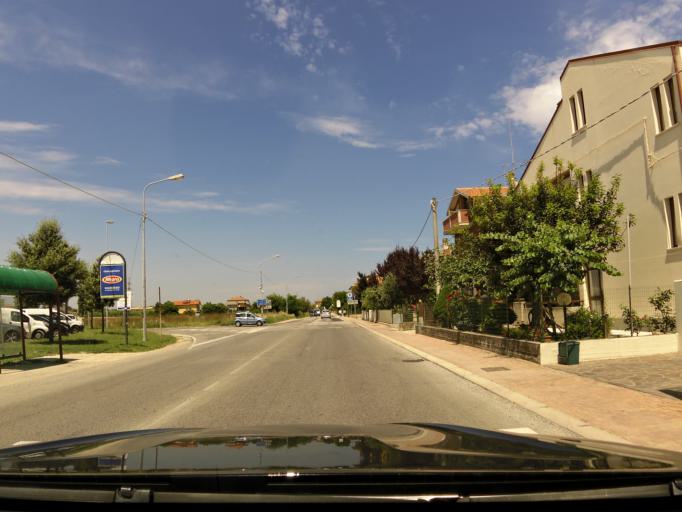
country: IT
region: The Marches
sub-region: Provincia di Ancona
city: Senigallia
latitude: 43.7377
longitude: 13.1879
